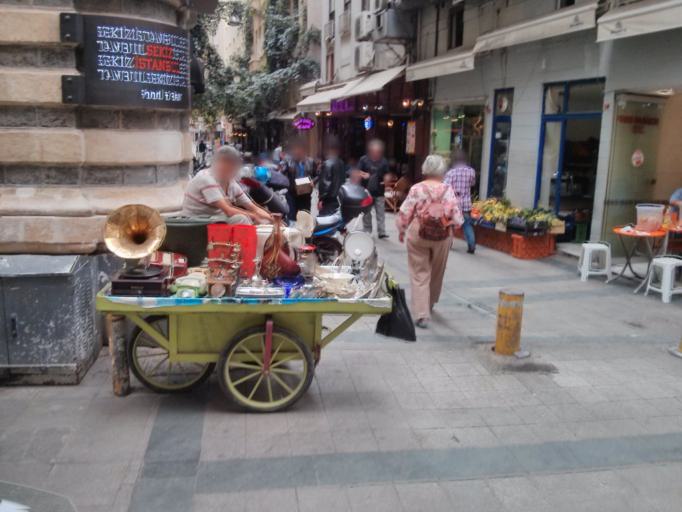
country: TR
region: Istanbul
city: Eminoenue
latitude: 41.0361
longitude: 28.9831
